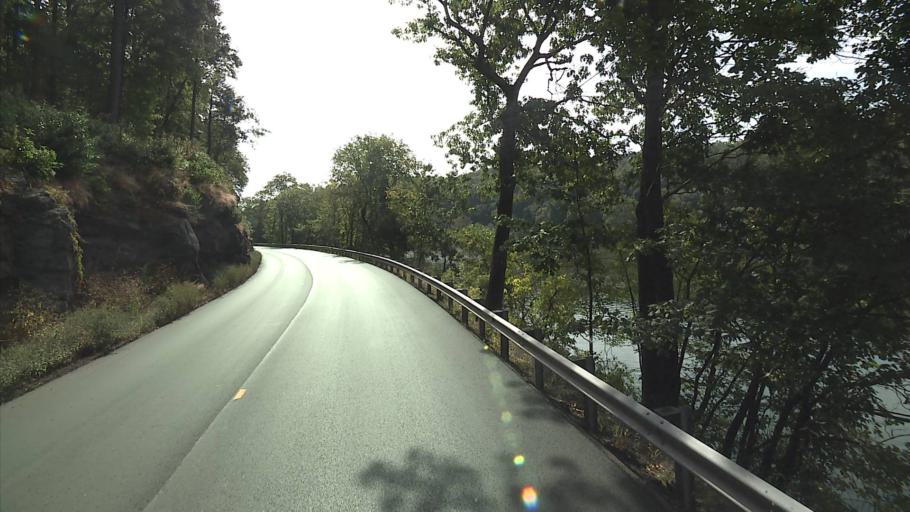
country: US
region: Connecticut
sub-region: Fairfield County
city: Shelton
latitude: 41.3346
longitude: -73.1161
